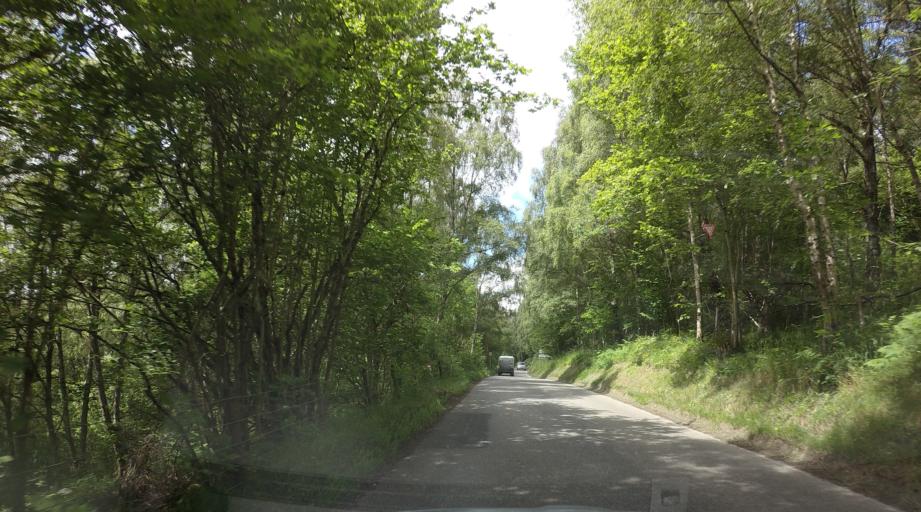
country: GB
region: Scotland
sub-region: Perth and Kinross
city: Aberfeldy
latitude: 56.7176
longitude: -3.9222
